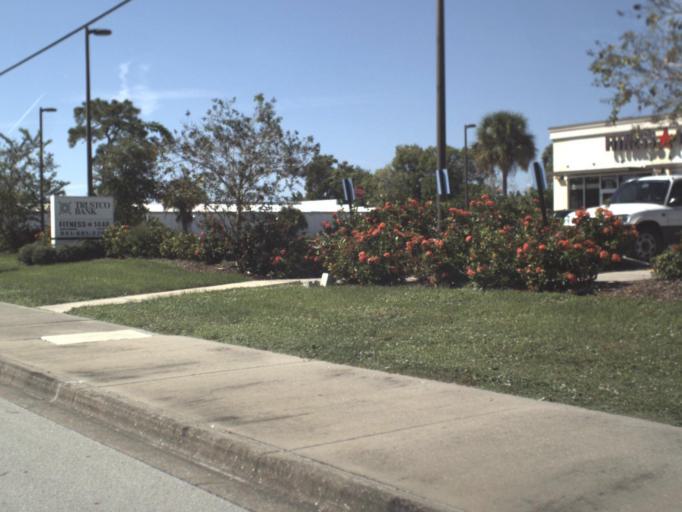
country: US
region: Florida
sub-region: Charlotte County
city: Grove City
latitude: 26.9347
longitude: -82.3110
